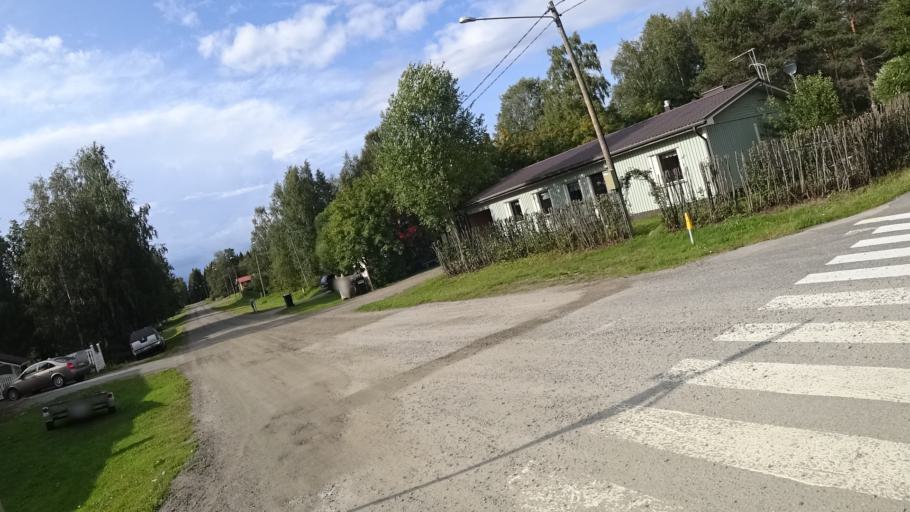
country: FI
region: North Karelia
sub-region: Joensuu
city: Ilomantsi
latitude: 62.6671
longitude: 30.9164
